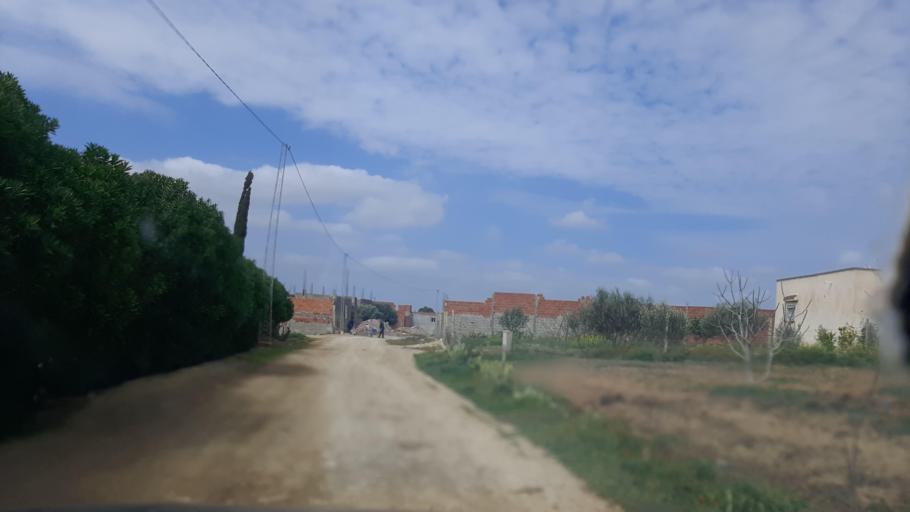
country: TN
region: Tunis
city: Oued Lill
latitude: 36.6871
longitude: 9.9982
